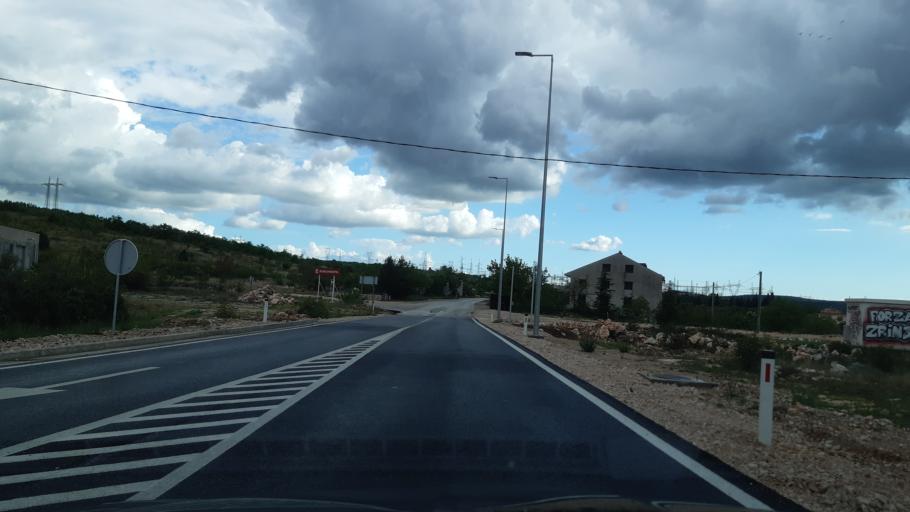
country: BA
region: Federation of Bosnia and Herzegovina
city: Rodoc
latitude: 43.3109
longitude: 17.7734
